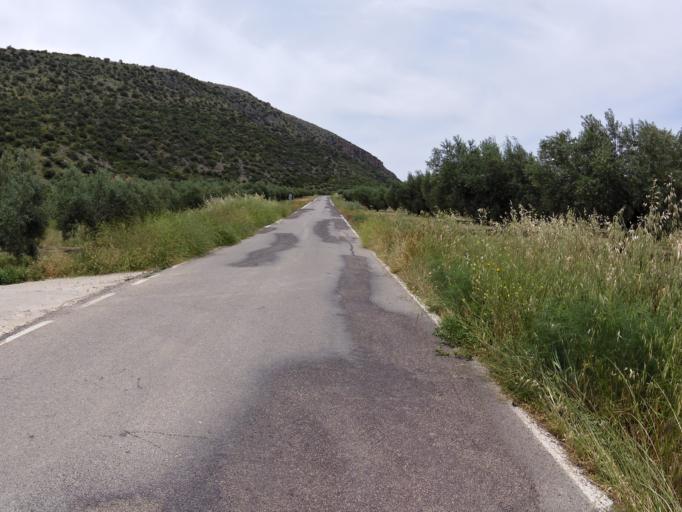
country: ES
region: Andalusia
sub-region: Province of Cordoba
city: Luque
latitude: 37.5195
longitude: -4.2247
